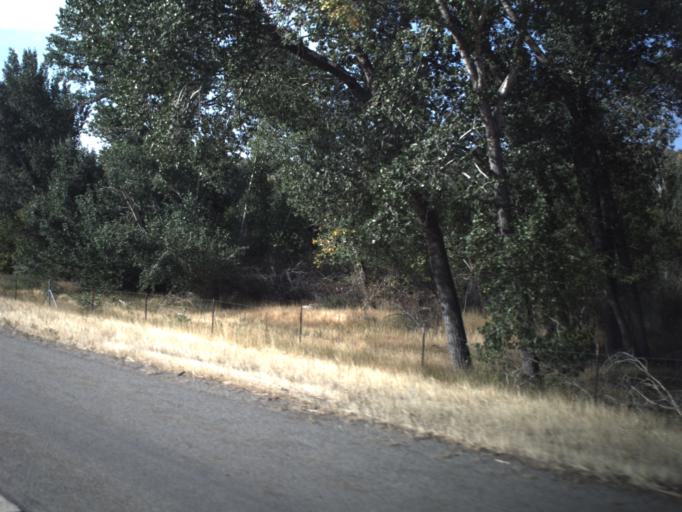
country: US
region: Utah
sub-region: Davis County
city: South Weber
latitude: 41.1445
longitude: -111.9585
